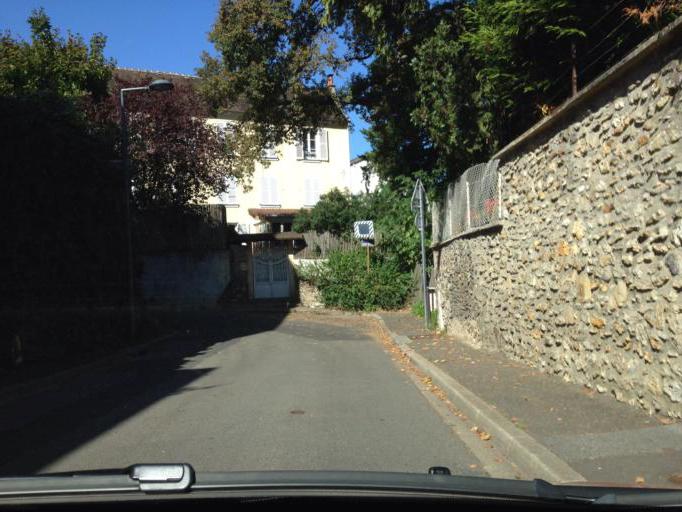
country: FR
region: Ile-de-France
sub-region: Departement des Hauts-de-Seine
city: Sevres
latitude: 48.8205
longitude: 2.2224
